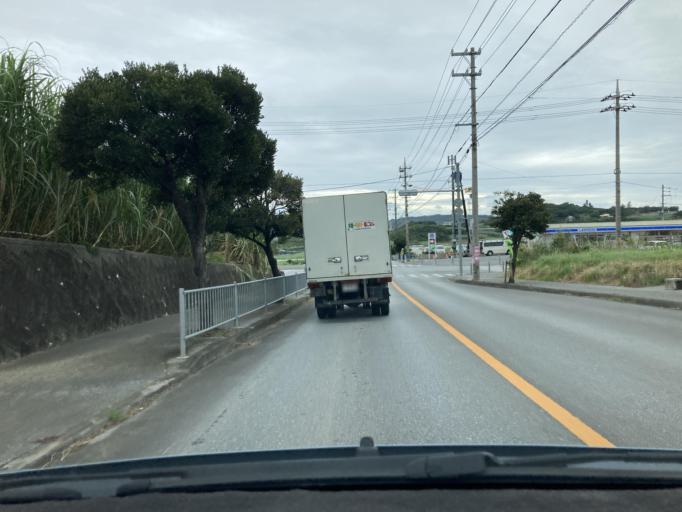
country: JP
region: Okinawa
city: Tomigusuku
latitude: 26.1614
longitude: 127.7083
